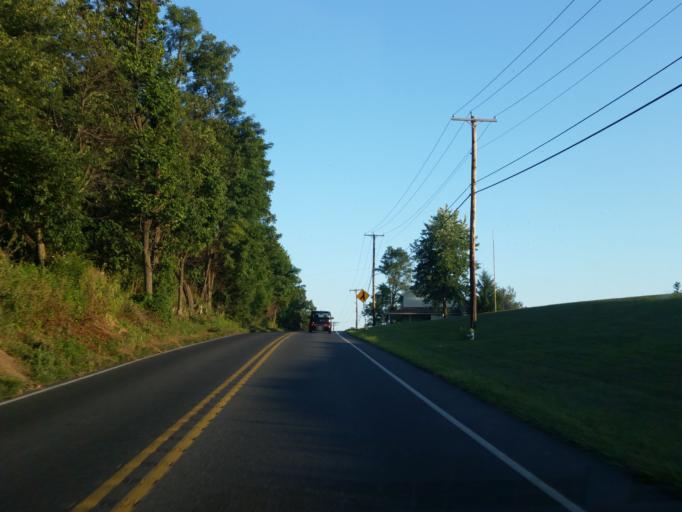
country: US
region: Pennsylvania
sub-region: Lebanon County
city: Sand Hill
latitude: 40.3716
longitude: -76.4329
